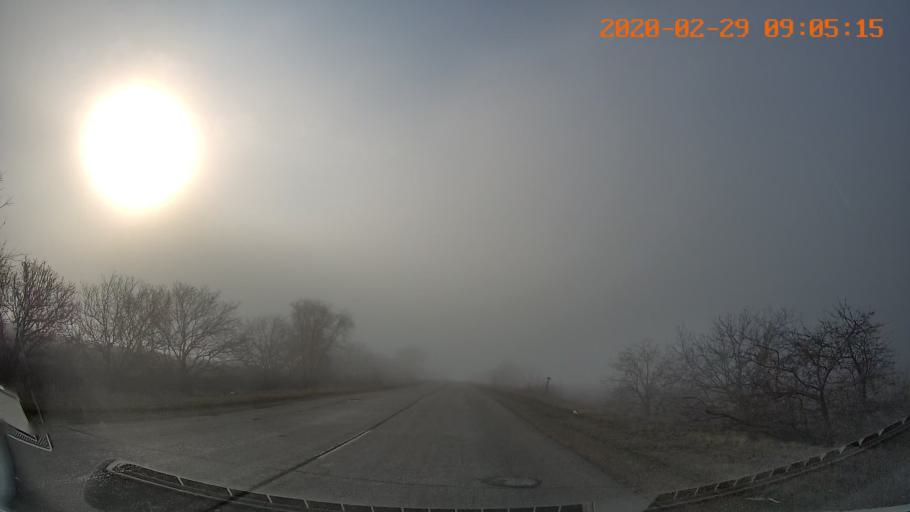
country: MD
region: Telenesti
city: Tiraspolul Nou
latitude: 46.8917
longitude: 29.7394
